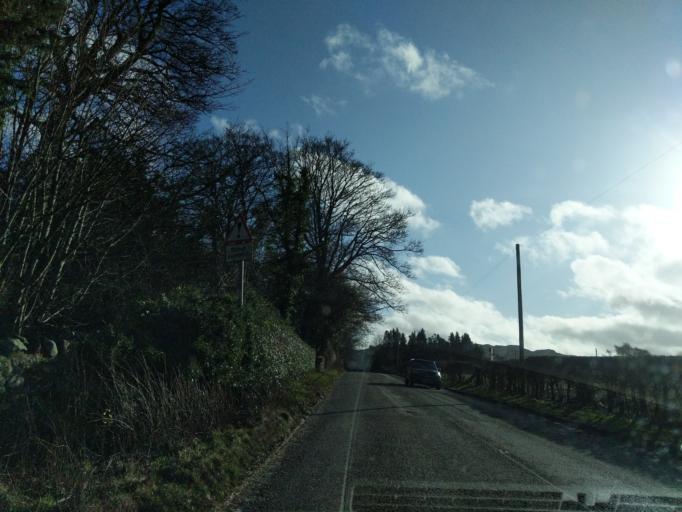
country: GB
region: Scotland
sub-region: Edinburgh
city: Ratho
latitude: 55.9011
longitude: -3.3879
